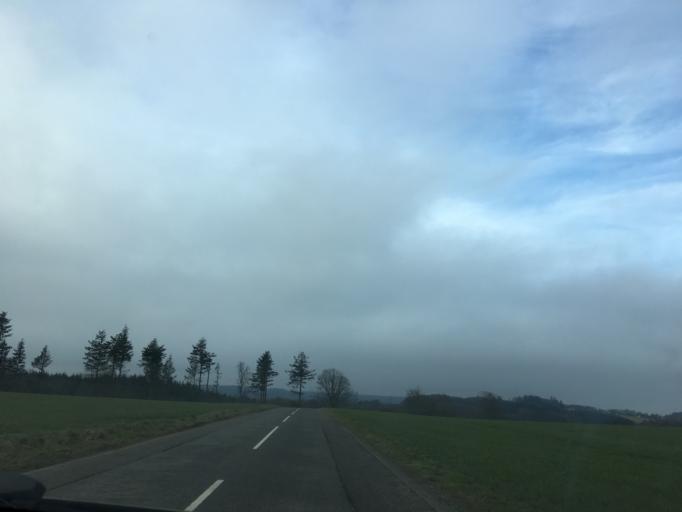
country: DK
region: South Denmark
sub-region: Vejle Kommune
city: Brejning
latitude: 55.7250
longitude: 9.6408
